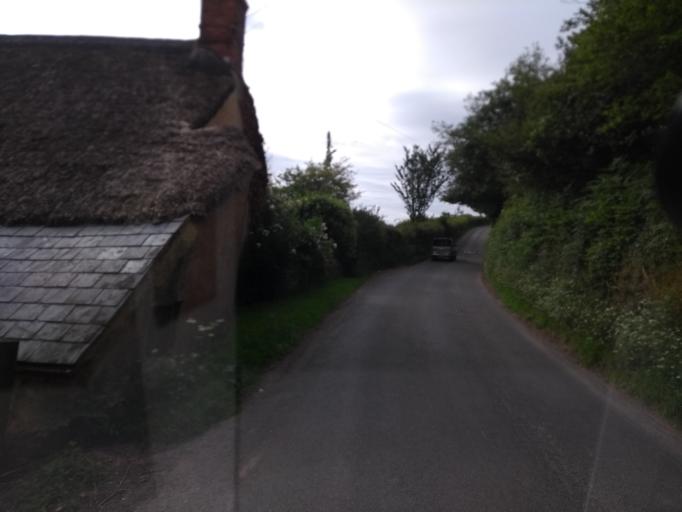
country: GB
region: England
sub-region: Somerset
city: Wiveliscombe
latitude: 51.0914
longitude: -3.3002
